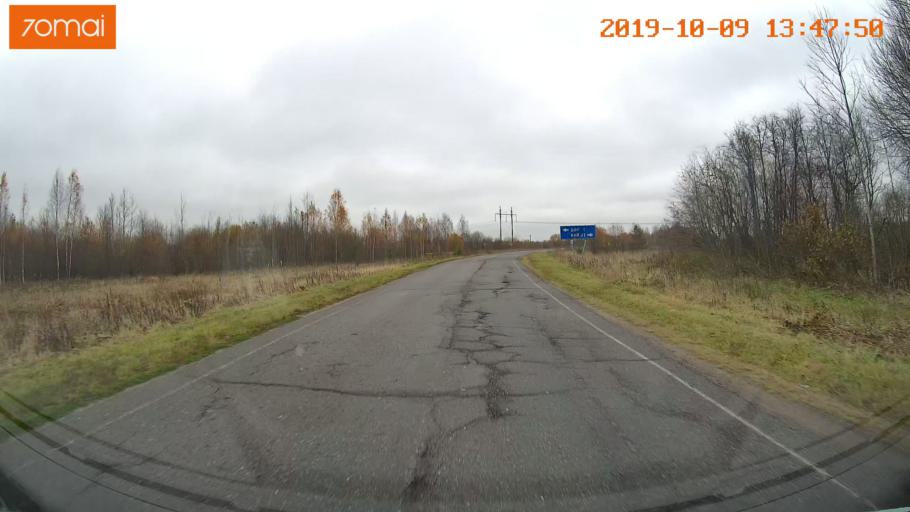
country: RU
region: Kostroma
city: Buy
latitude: 58.3958
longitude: 41.2266
